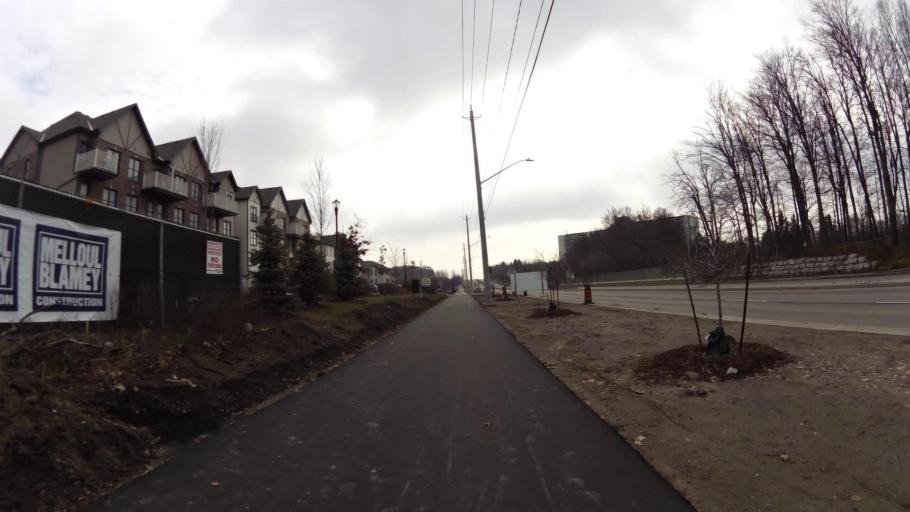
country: CA
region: Ontario
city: Kitchener
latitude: 43.4170
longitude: -80.4693
